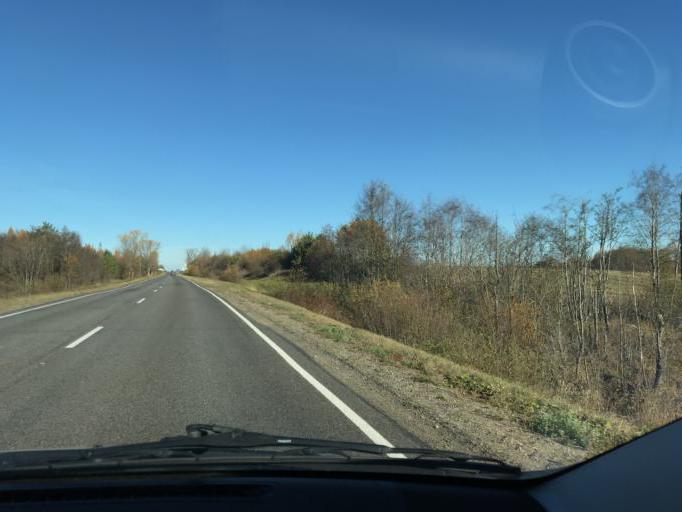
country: BY
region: Vitebsk
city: Lyepyel'
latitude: 55.0335
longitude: 28.7477
